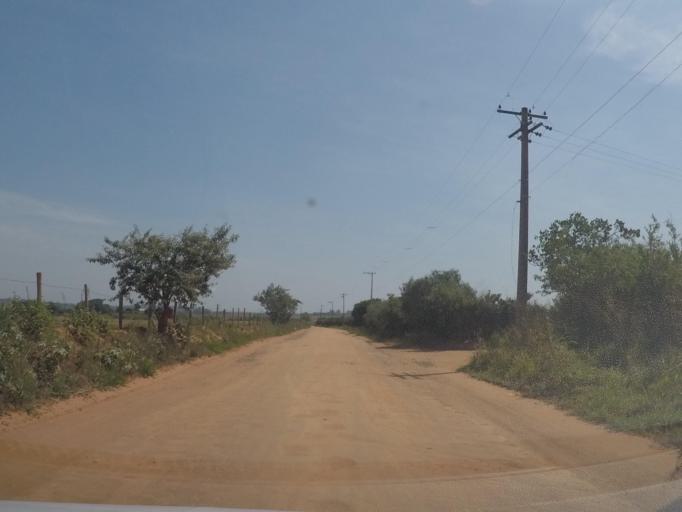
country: BR
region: Sao Paulo
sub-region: Sumare
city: Sumare
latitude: -22.8605
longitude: -47.2767
